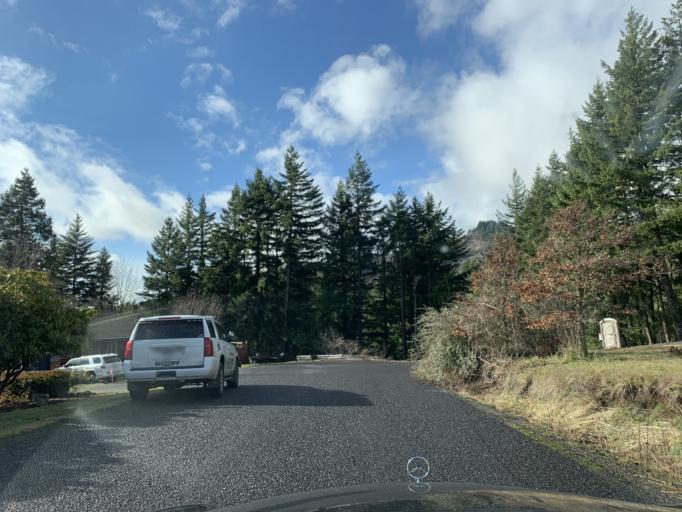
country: US
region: Washington
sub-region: Skamania County
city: Carson
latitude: 45.7215
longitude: -121.8176
